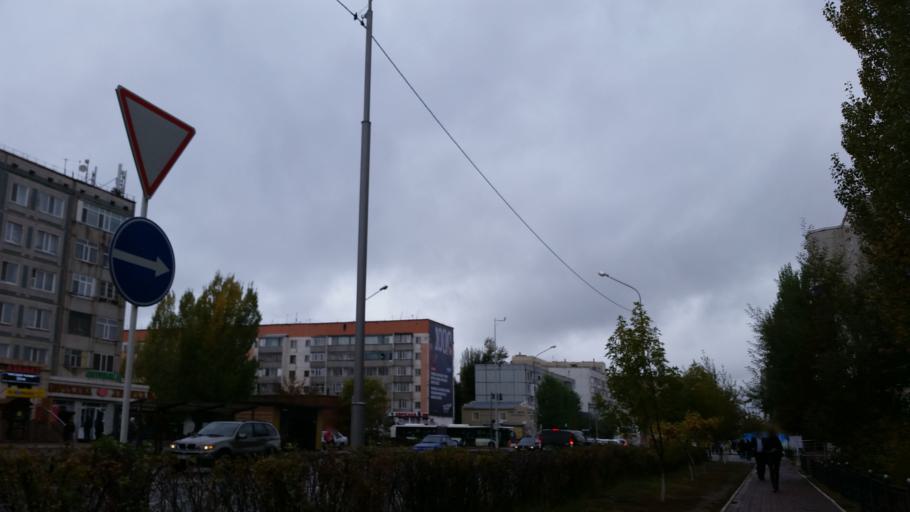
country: KZ
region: Astana Qalasy
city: Astana
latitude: 51.1546
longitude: 71.5045
